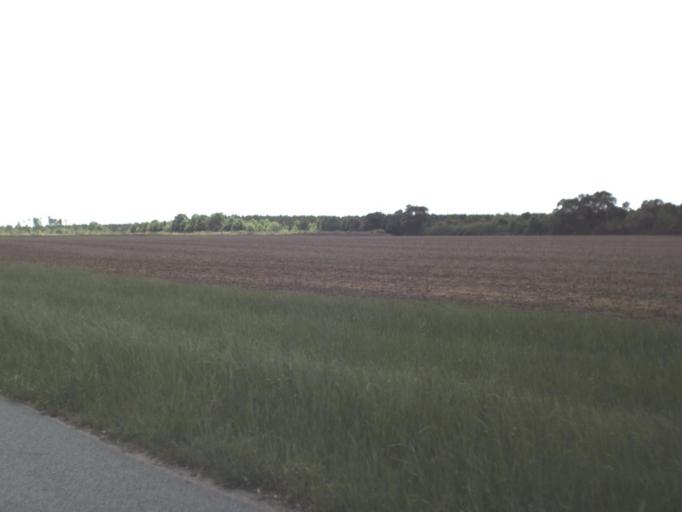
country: US
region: Florida
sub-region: Escambia County
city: Molino
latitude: 30.8377
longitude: -87.4352
